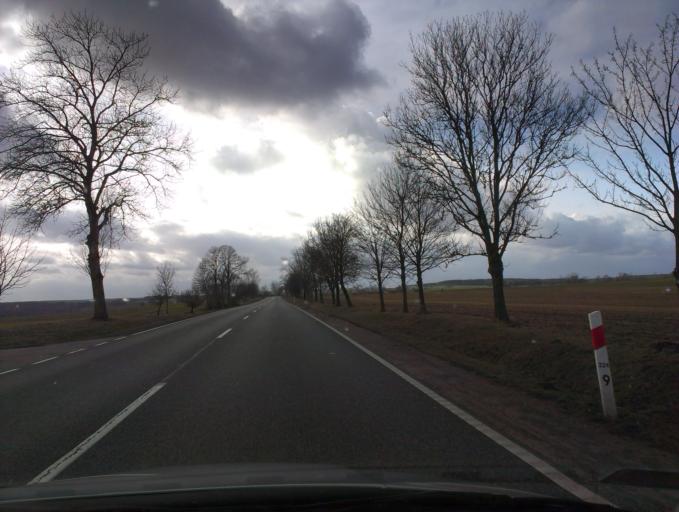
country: PL
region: Pomeranian Voivodeship
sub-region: Powiat czluchowski
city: Debrzno
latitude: 53.6290
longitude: 17.2481
